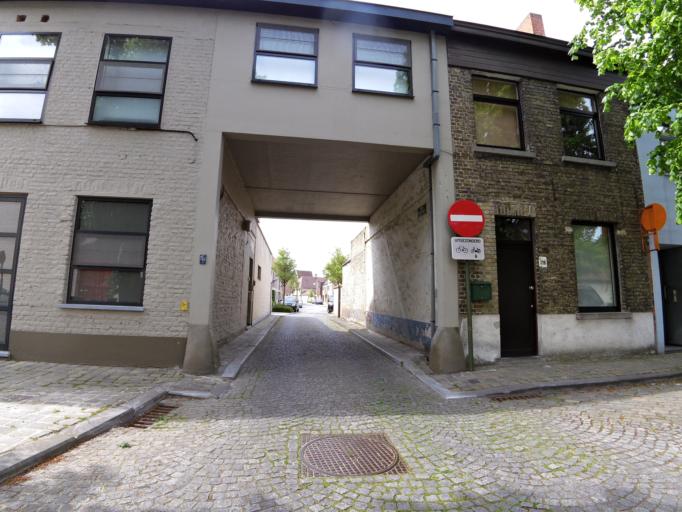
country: BE
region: Flanders
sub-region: Provincie West-Vlaanderen
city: Brugge
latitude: 51.2173
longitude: 3.2237
